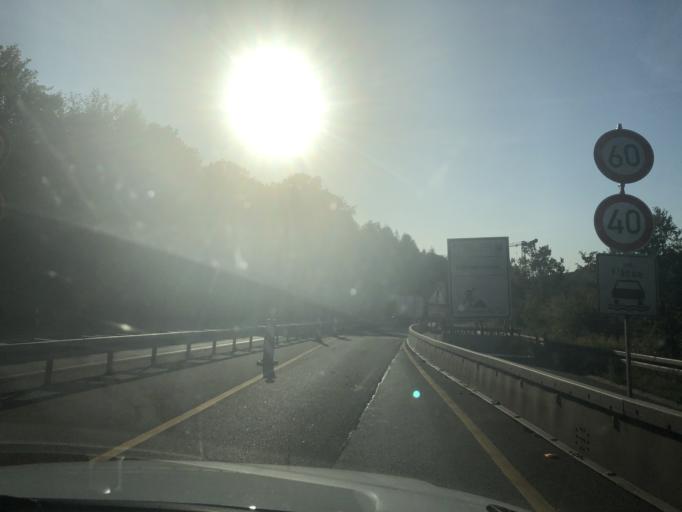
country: DE
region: Saarland
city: Eppelborn
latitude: 49.4127
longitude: 6.9960
